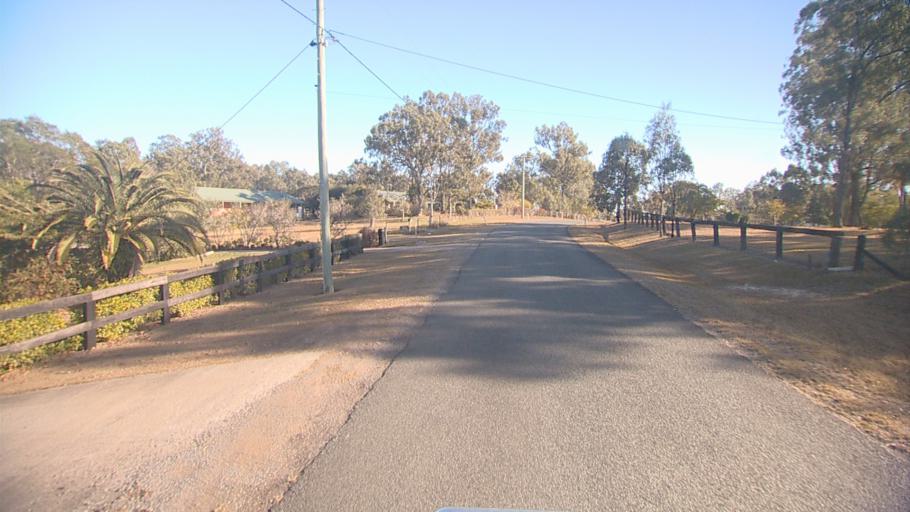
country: AU
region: Queensland
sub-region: Logan
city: Cedar Vale
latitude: -27.8343
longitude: 153.0065
